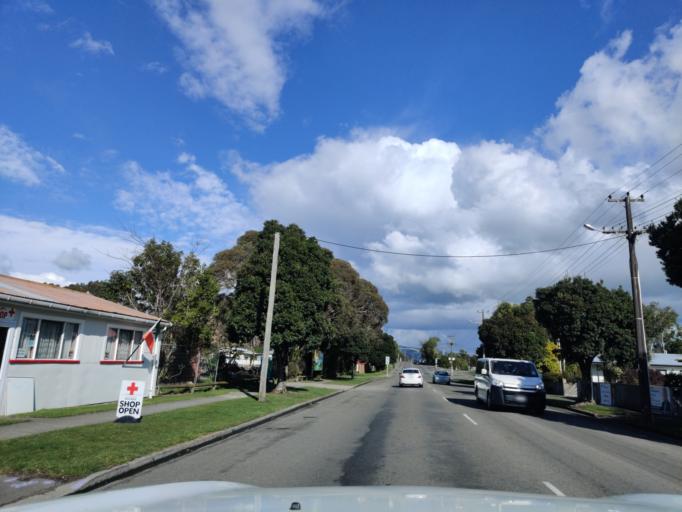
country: NZ
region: Manawatu-Wanganui
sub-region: Palmerston North City
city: Palmerston North
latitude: -40.2942
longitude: 175.7537
